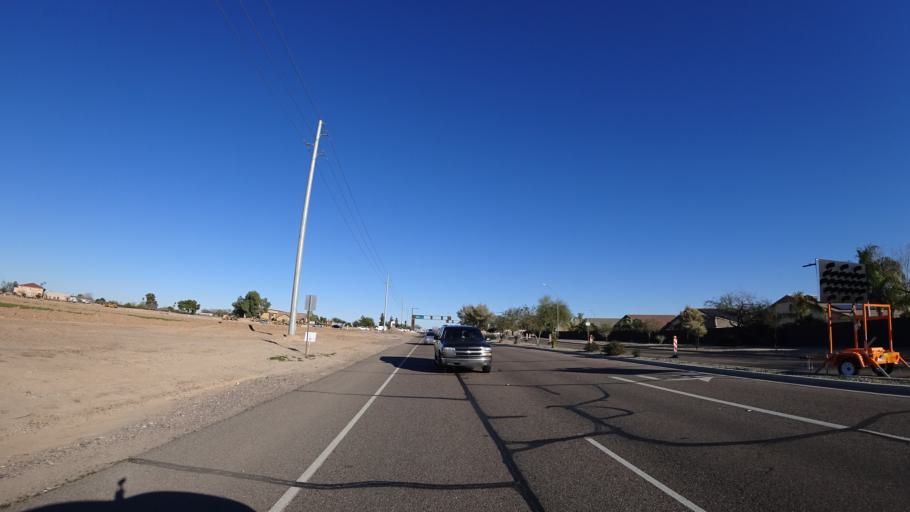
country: US
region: Arizona
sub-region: Maricopa County
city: Goodyear
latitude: 33.4502
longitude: -112.4112
